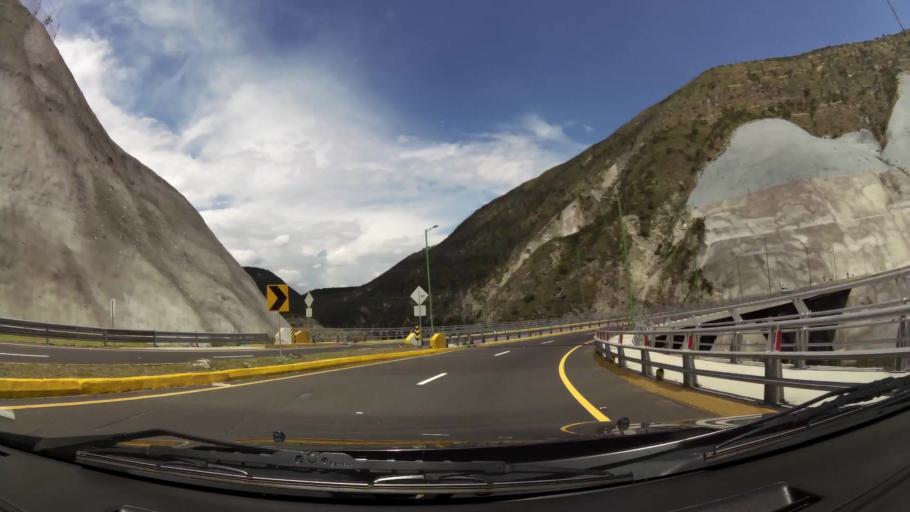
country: EC
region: Pichincha
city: Quito
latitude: -0.1048
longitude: -78.3819
